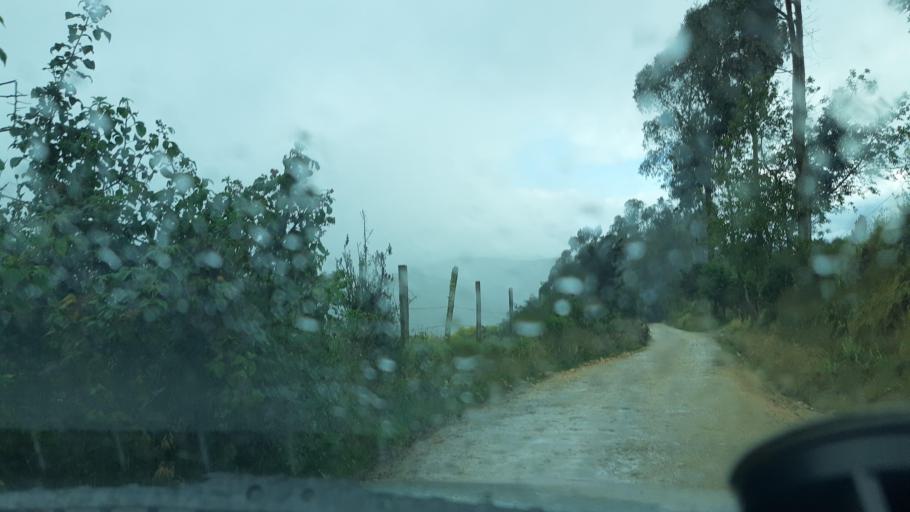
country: CO
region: Cundinamarca
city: Villapinzon
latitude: 5.2112
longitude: -73.5702
